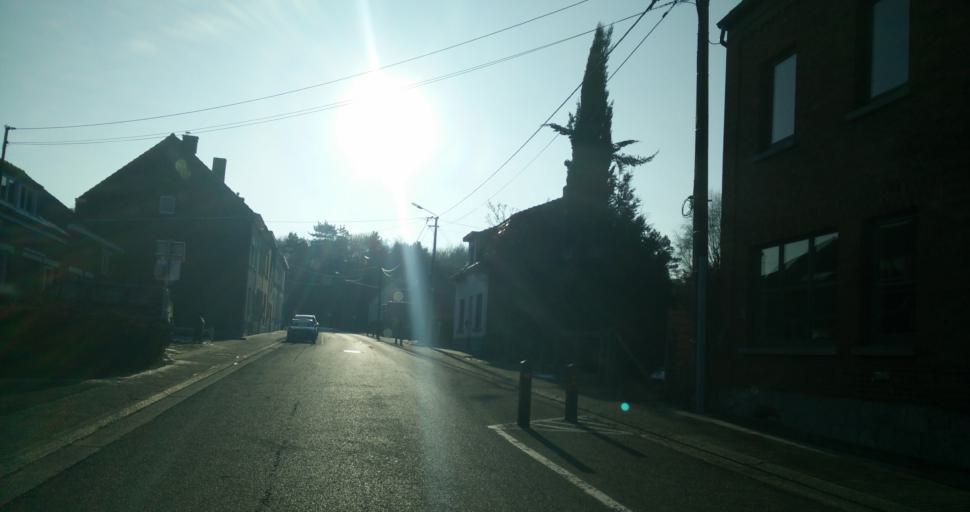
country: BE
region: Wallonia
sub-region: Province du Brabant Wallon
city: Braine-le-Chateau
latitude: 50.6758
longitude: 4.2656
